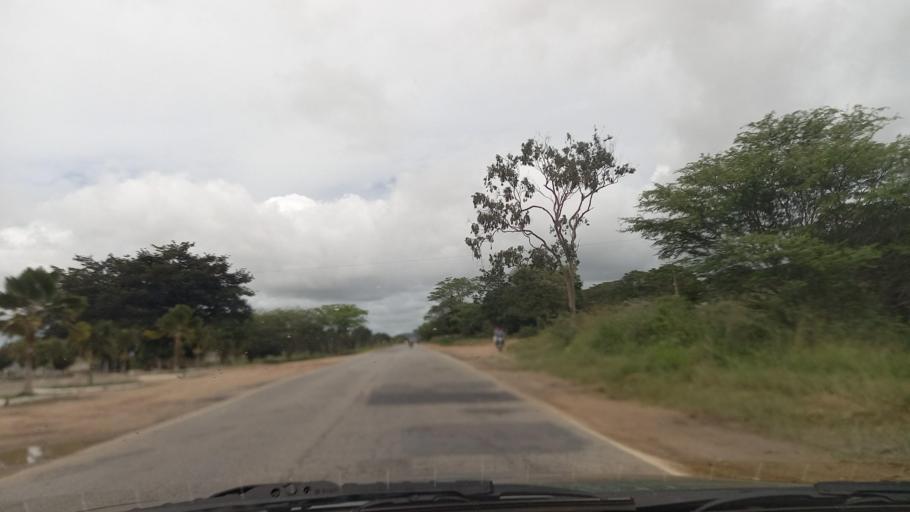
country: BR
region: Pernambuco
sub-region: Sao Joao
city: Sao Joao
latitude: -8.8797
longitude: -36.4249
